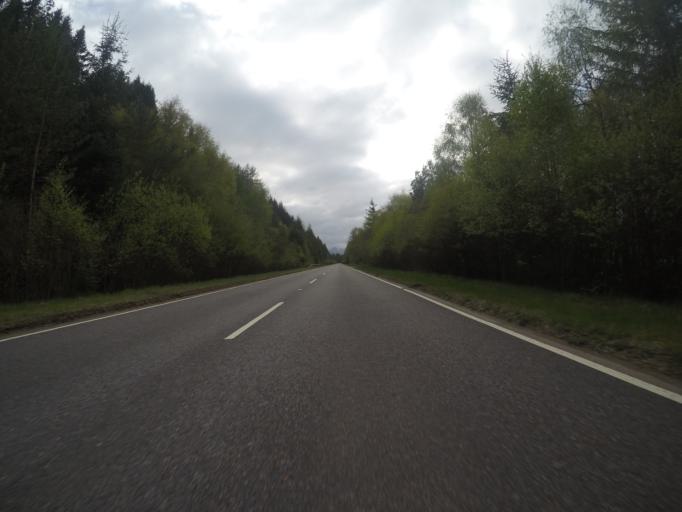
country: GB
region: Scotland
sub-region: Highland
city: Spean Bridge
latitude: 57.1687
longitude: -4.8414
